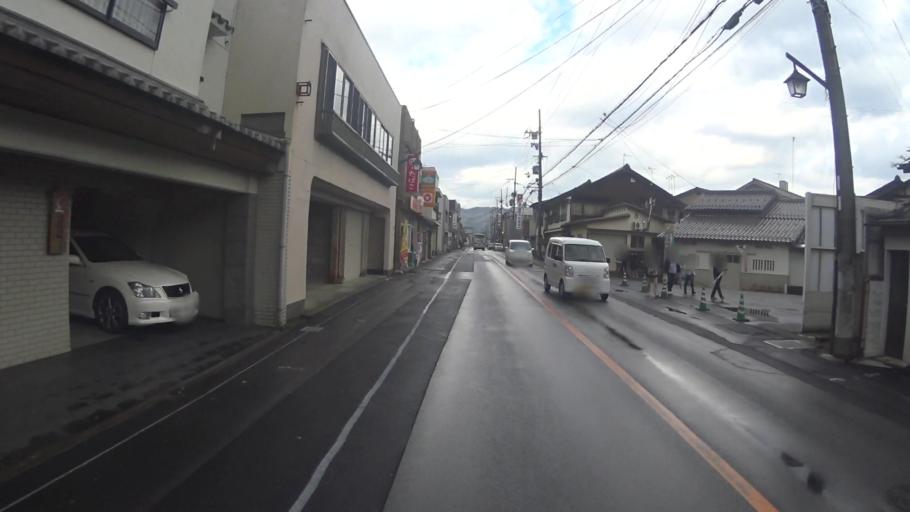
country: JP
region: Kyoto
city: Miyazu
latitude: 35.5568
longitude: 135.1836
